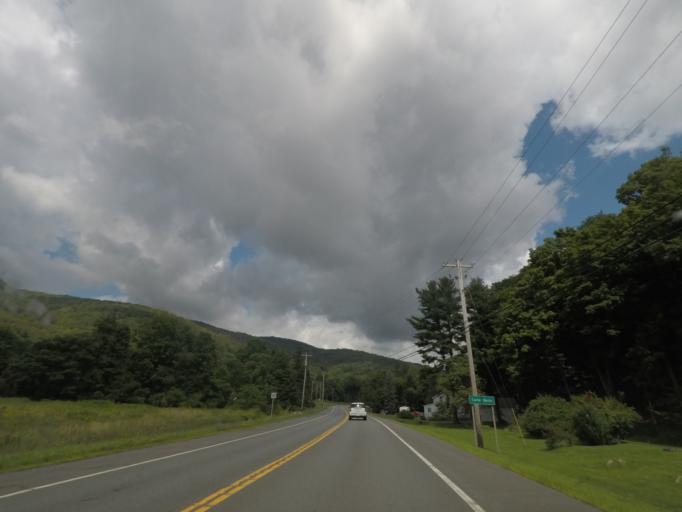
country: US
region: Massachusetts
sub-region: Berkshire County
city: Williamstown
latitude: 42.6596
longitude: -73.3673
